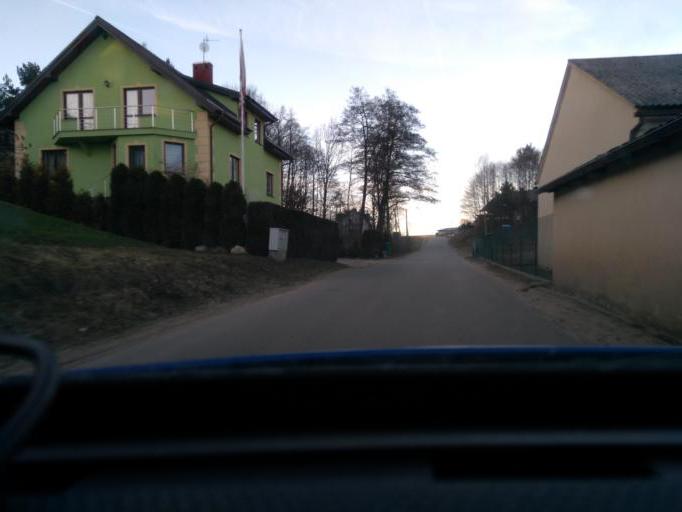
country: PL
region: Pomeranian Voivodeship
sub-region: Powiat kartuski
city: Przodkowo
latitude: 54.3847
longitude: 18.2694
